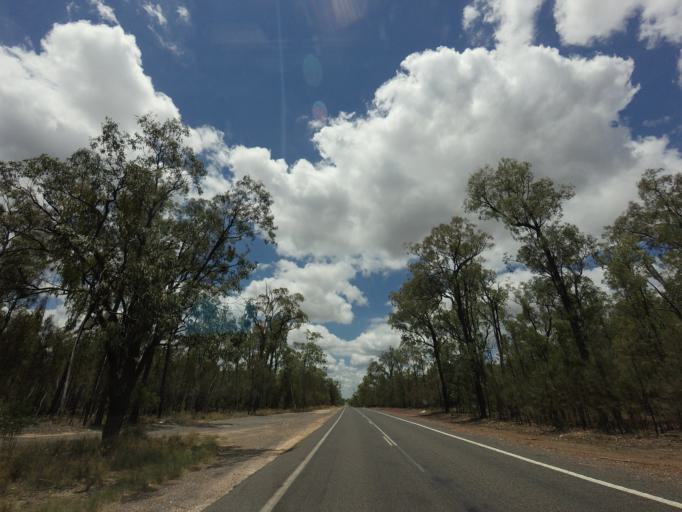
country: AU
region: Queensland
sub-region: Goondiwindi
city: Goondiwindi
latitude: -28.0300
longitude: 150.8327
